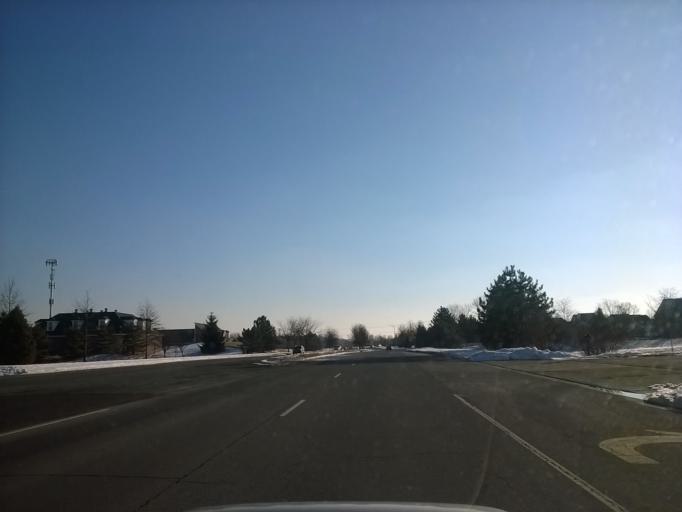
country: US
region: Indiana
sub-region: Hamilton County
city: Carmel
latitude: 39.9745
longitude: -86.0706
